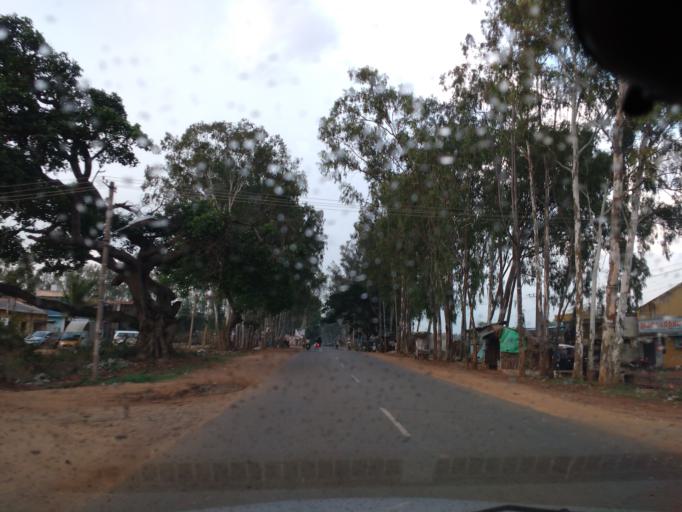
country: IN
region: Karnataka
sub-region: Tumkur
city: Tiptur
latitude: 13.2630
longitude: 76.4939
